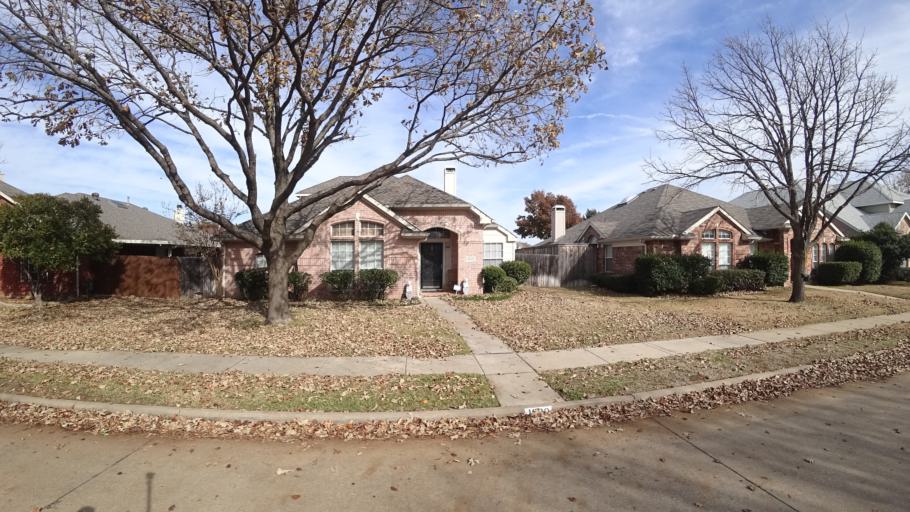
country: US
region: Texas
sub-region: Denton County
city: Highland Village
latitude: 33.0650
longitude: -97.0394
